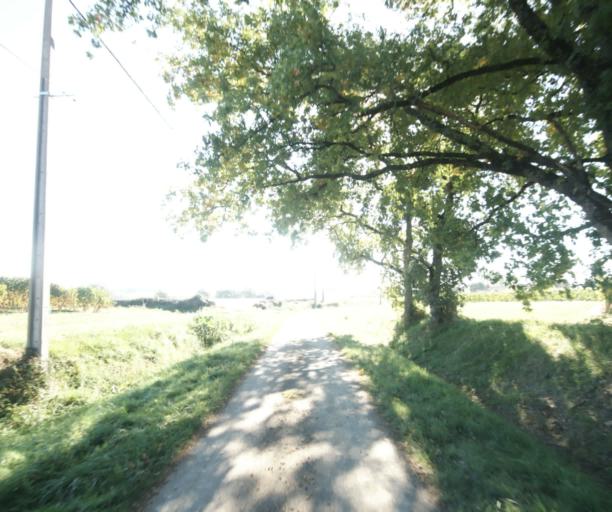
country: FR
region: Midi-Pyrenees
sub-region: Departement du Gers
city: Gondrin
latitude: 43.8329
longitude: 0.2373
